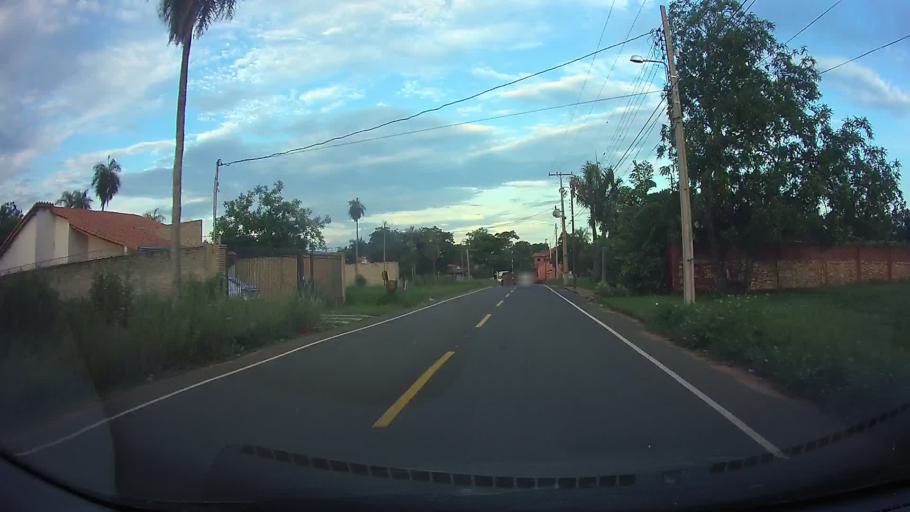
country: PY
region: Central
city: San Lorenzo
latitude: -25.2548
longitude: -57.5016
